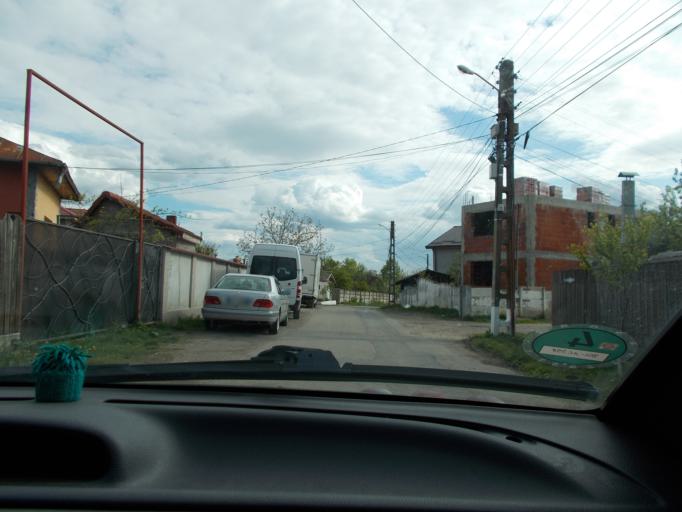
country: RO
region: Ilfov
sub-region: Comuna Branesti
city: Branesti
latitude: 44.4553
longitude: 26.3331
